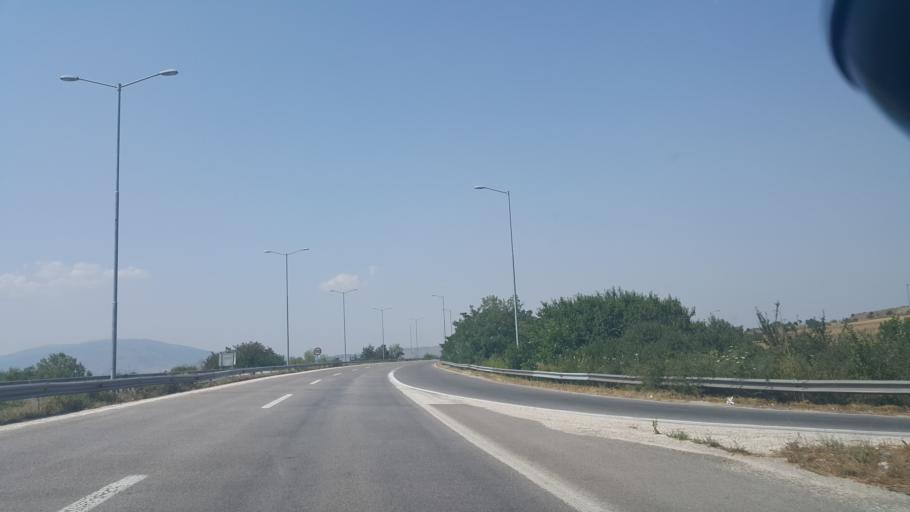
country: MK
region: Petrovec
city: Petrovec
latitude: 41.9359
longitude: 21.6266
